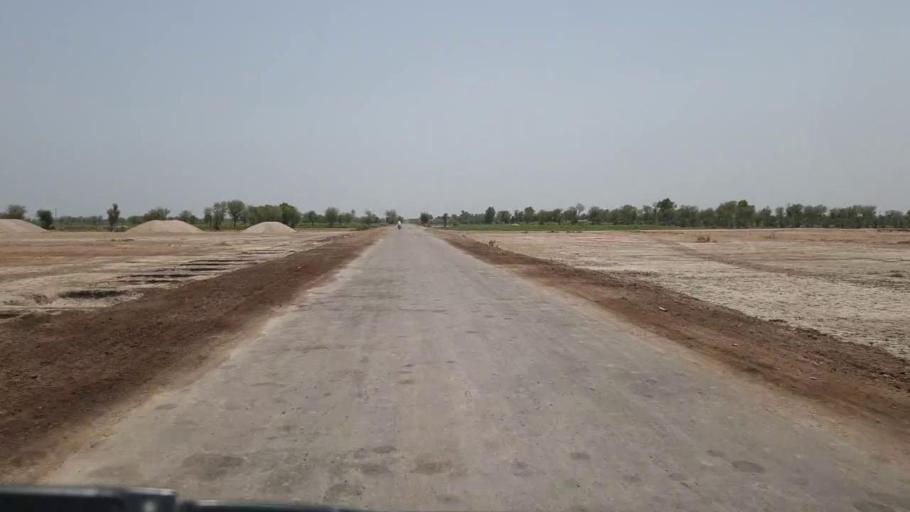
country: PK
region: Sindh
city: Daulatpur
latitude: 26.4499
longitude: 68.1170
